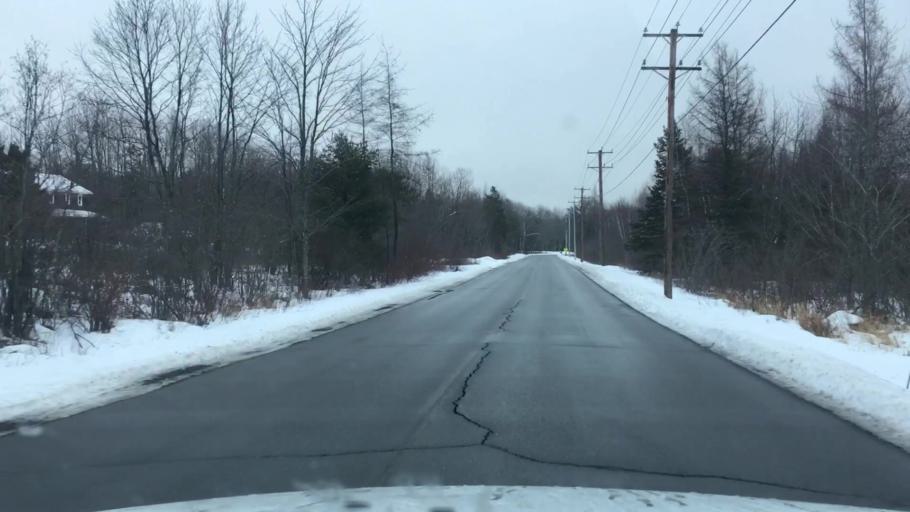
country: US
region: Maine
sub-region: Hancock County
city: Trenton
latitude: 44.4079
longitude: -68.3258
